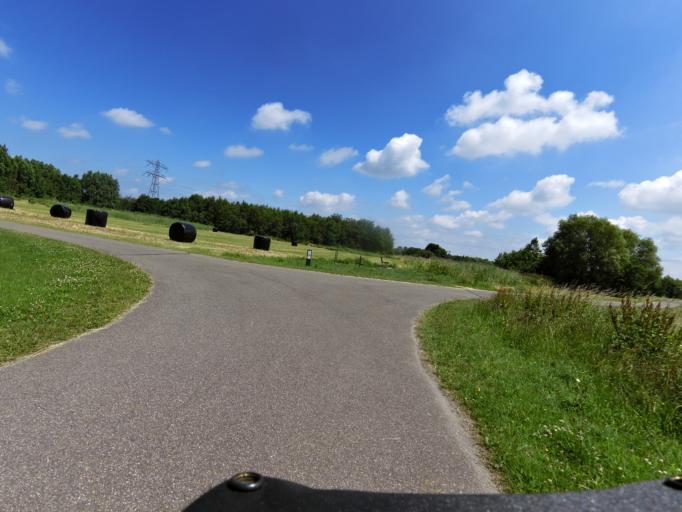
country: NL
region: South Holland
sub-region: Gemeente Delft
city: Delft
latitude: 51.9721
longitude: 4.3710
